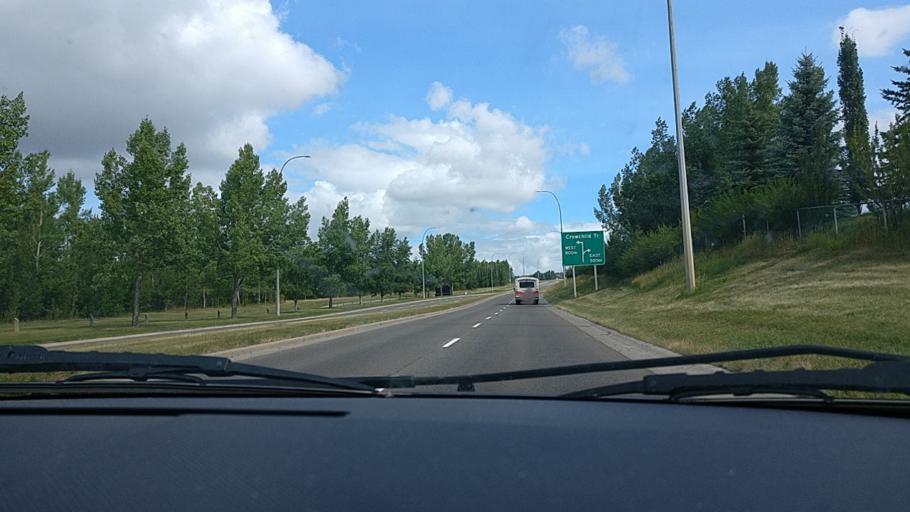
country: CA
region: Alberta
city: Calgary
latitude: 51.1050
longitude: -114.1811
